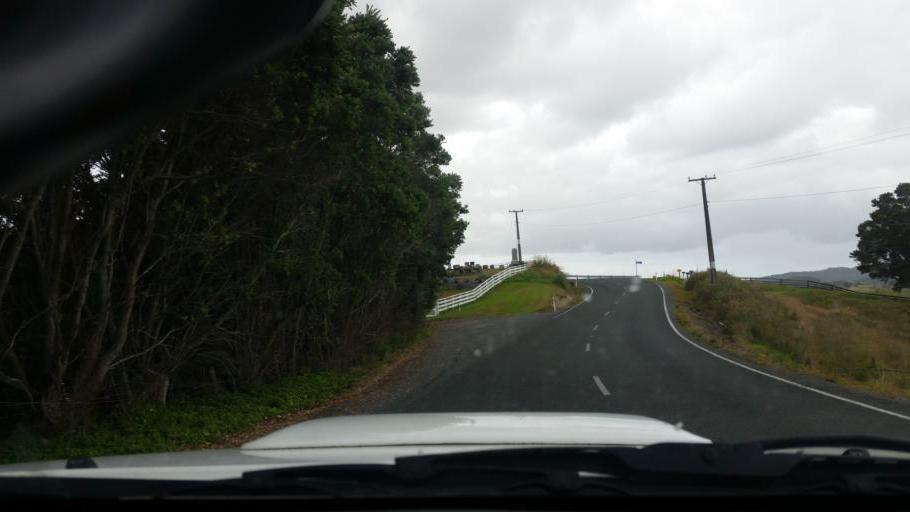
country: NZ
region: Northland
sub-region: Whangarei
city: Ruakaka
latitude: -36.1033
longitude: 174.3504
